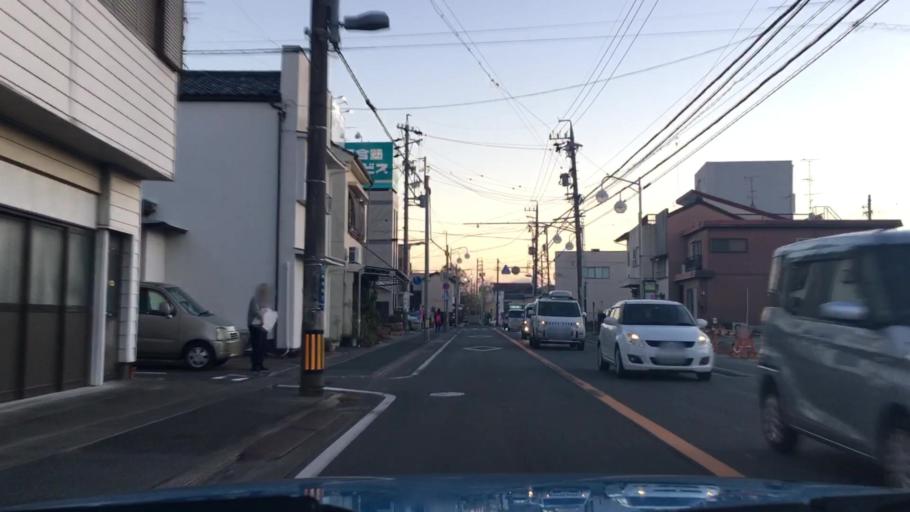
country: JP
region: Shizuoka
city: Hamamatsu
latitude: 34.7152
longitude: 137.7210
